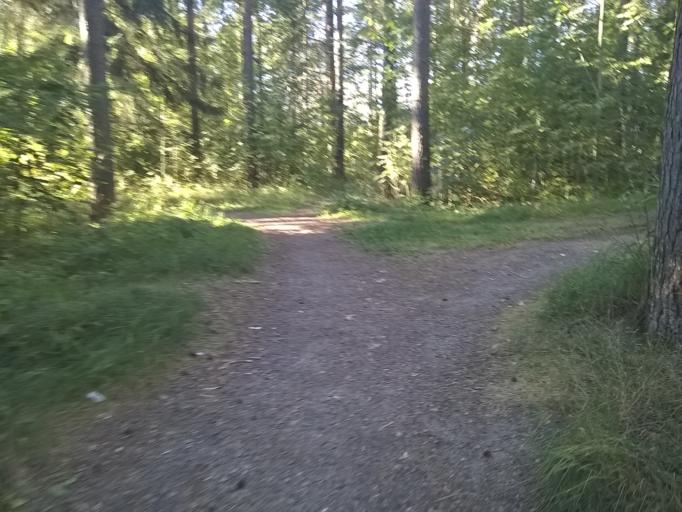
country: FI
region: Pirkanmaa
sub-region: Tampere
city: Tampere
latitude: 61.4464
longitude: 23.8448
